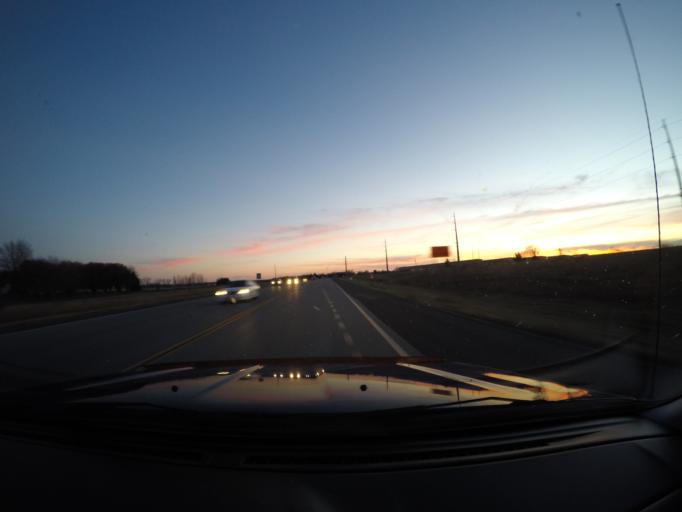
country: US
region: Kansas
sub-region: Douglas County
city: Lawrence
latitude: 38.9483
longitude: -95.3368
